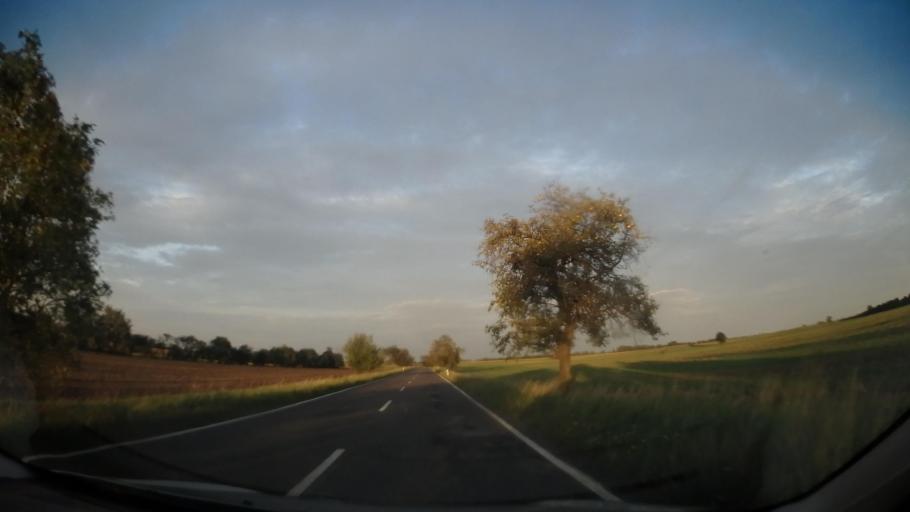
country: CZ
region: Central Bohemia
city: Milovice
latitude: 50.2253
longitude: 14.9056
